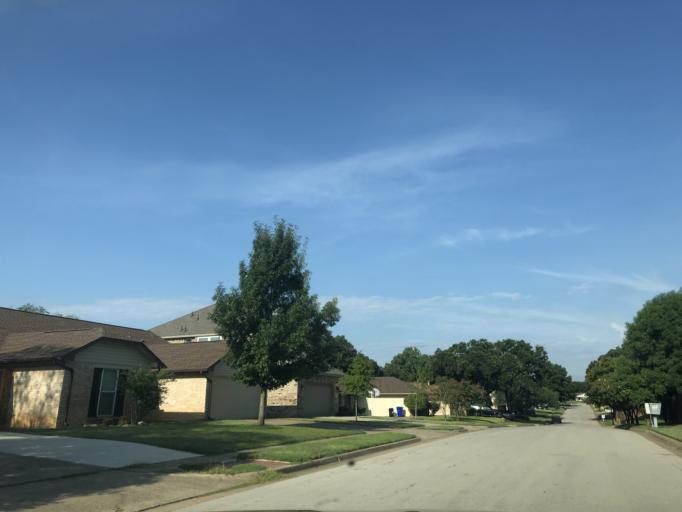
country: US
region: Texas
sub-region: Tarrant County
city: Euless
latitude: 32.8740
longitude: -97.0847
